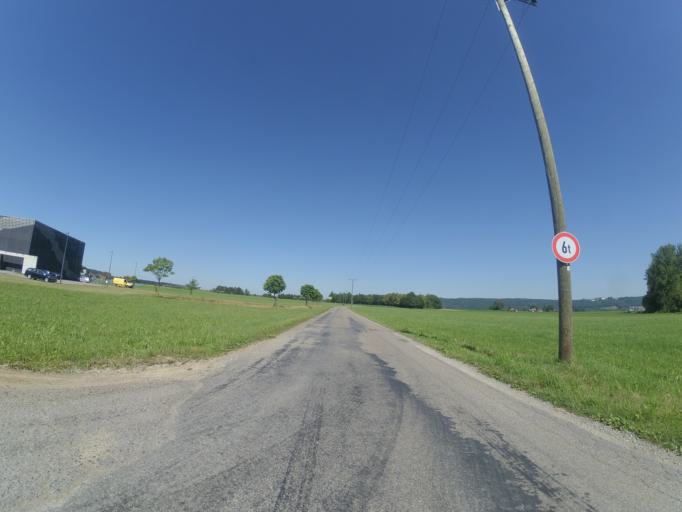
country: DE
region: Baden-Wuerttemberg
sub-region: Tuebingen Region
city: Leutkirch im Allgau
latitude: 47.8352
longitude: 10.0072
